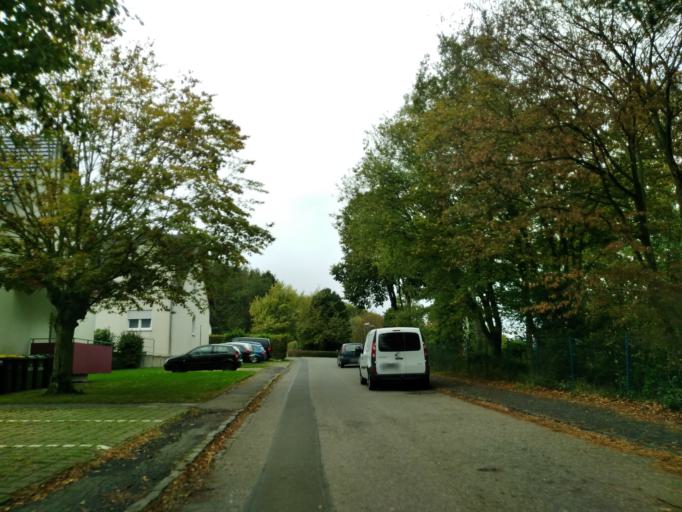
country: DE
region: Rheinland-Pfalz
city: Windhagen
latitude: 50.6618
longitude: 7.3002
